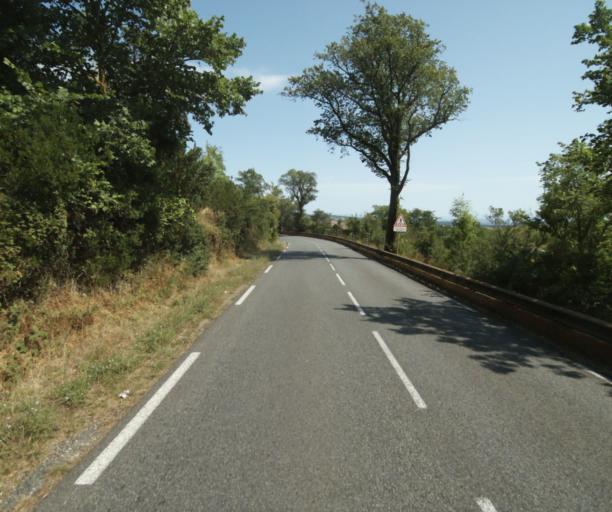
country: FR
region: Midi-Pyrenees
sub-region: Departement de la Haute-Garonne
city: Saint-Felix-Lauragais
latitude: 43.4473
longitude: 1.8883
